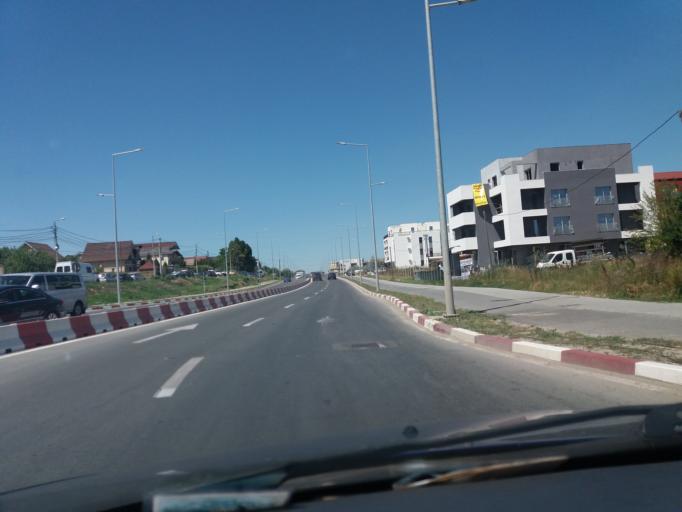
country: RO
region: Constanta
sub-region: Comuna Navodari
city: Navodari
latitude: 44.2918
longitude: 28.6194
